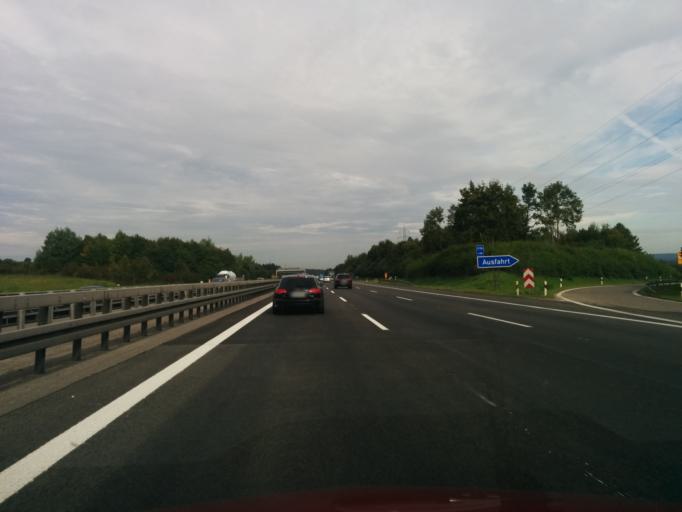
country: DE
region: Baden-Wuerttemberg
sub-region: Regierungsbezirk Stuttgart
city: Kirchheim unter Teck
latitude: 48.6394
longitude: 9.4342
